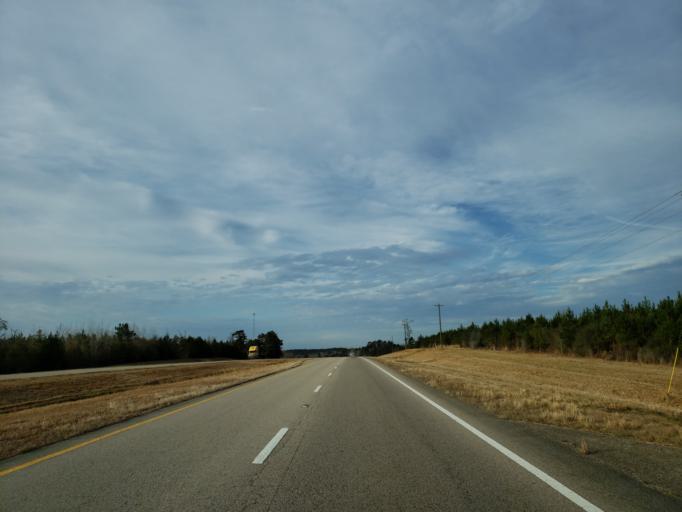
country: US
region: Mississippi
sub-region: Wayne County
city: Waynesboro
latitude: 31.7736
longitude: -88.6742
